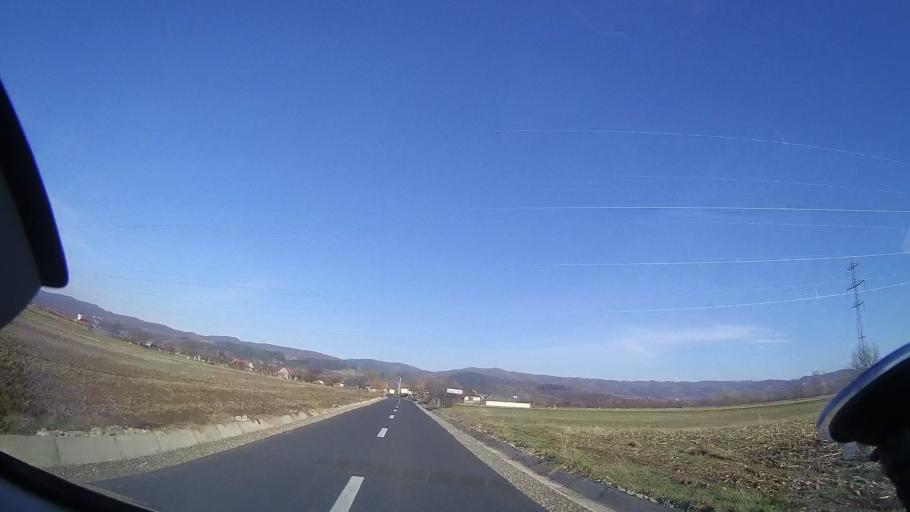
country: RO
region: Bihor
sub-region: Comuna Auseu
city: Auseu
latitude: 47.0179
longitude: 22.4923
